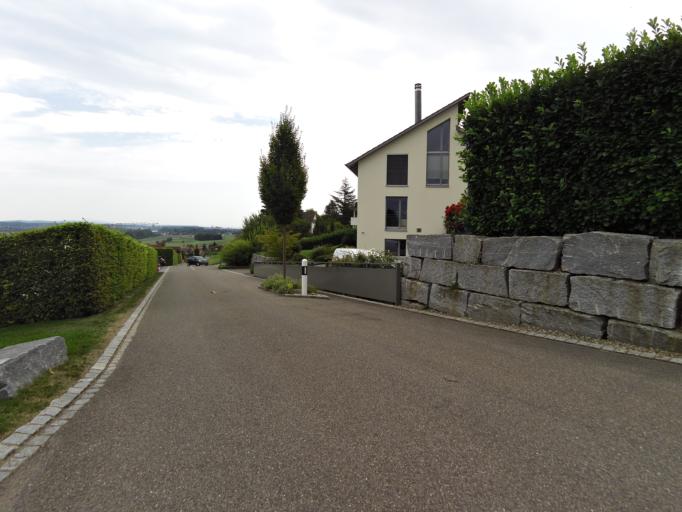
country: CH
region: Thurgau
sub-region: Kreuzlingen District
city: Ermatingen
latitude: 47.6604
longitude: 9.1056
